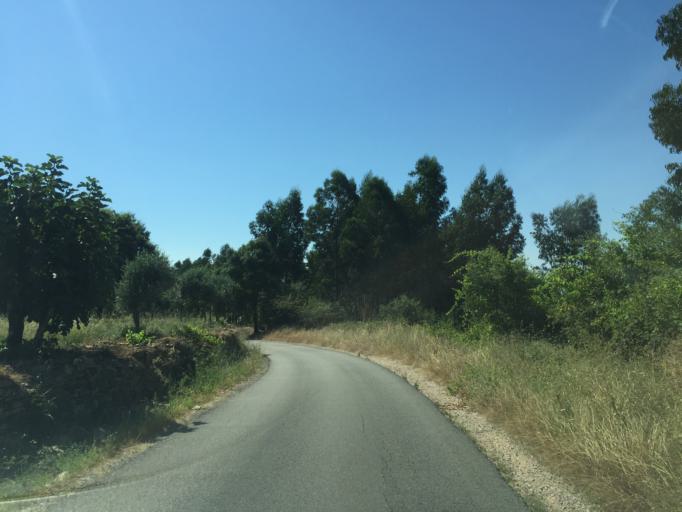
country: PT
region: Santarem
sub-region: Ferreira do Zezere
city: Ferreira do Zezere
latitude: 39.5928
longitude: -8.2869
